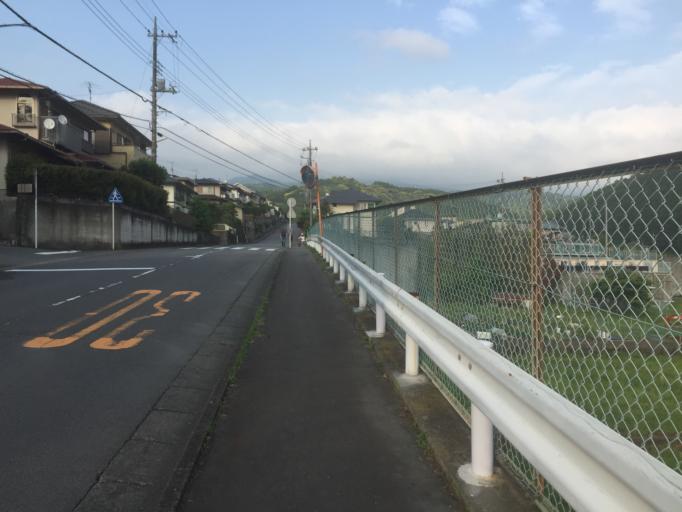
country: JP
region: Shizuoka
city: Mishima
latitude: 35.1781
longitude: 138.9306
